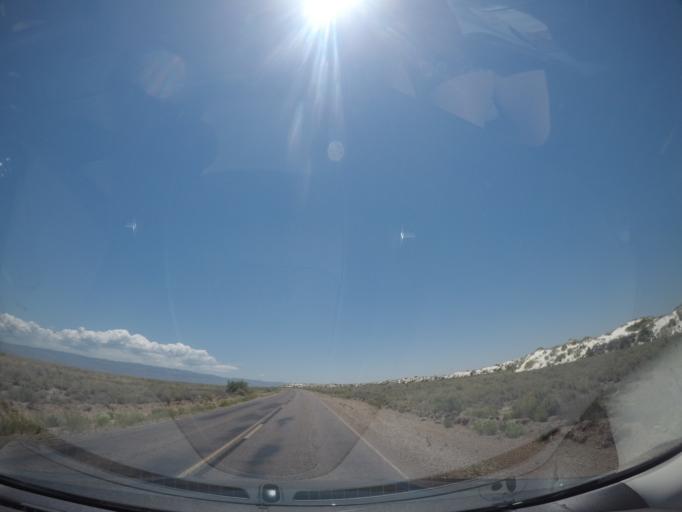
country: US
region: New Mexico
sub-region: Otero County
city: Holloman Air Force Base
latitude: 32.7894
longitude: -106.1930
